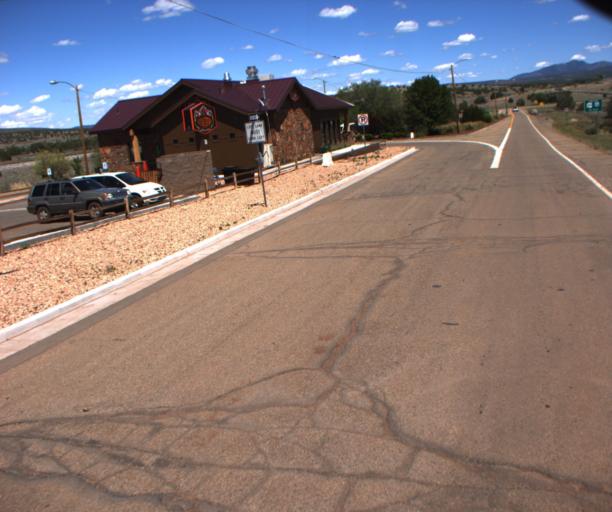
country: US
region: Arizona
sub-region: Coconino County
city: Williams
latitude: 35.2227
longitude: -112.4787
